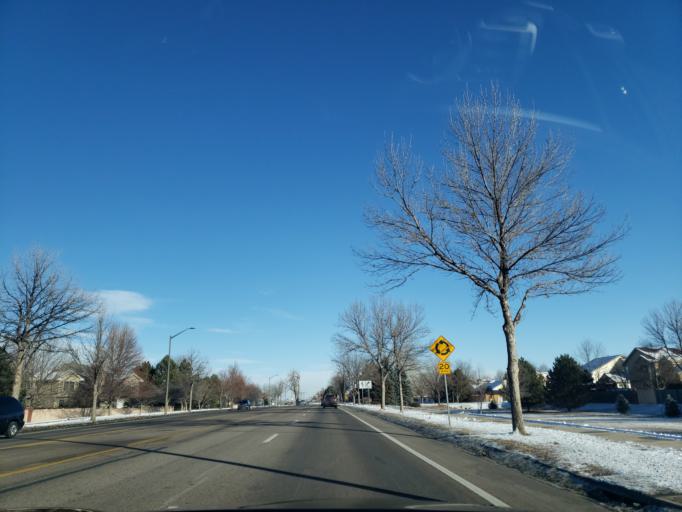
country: US
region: Colorado
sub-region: Larimer County
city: Fort Collins
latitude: 40.5378
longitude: -105.0237
